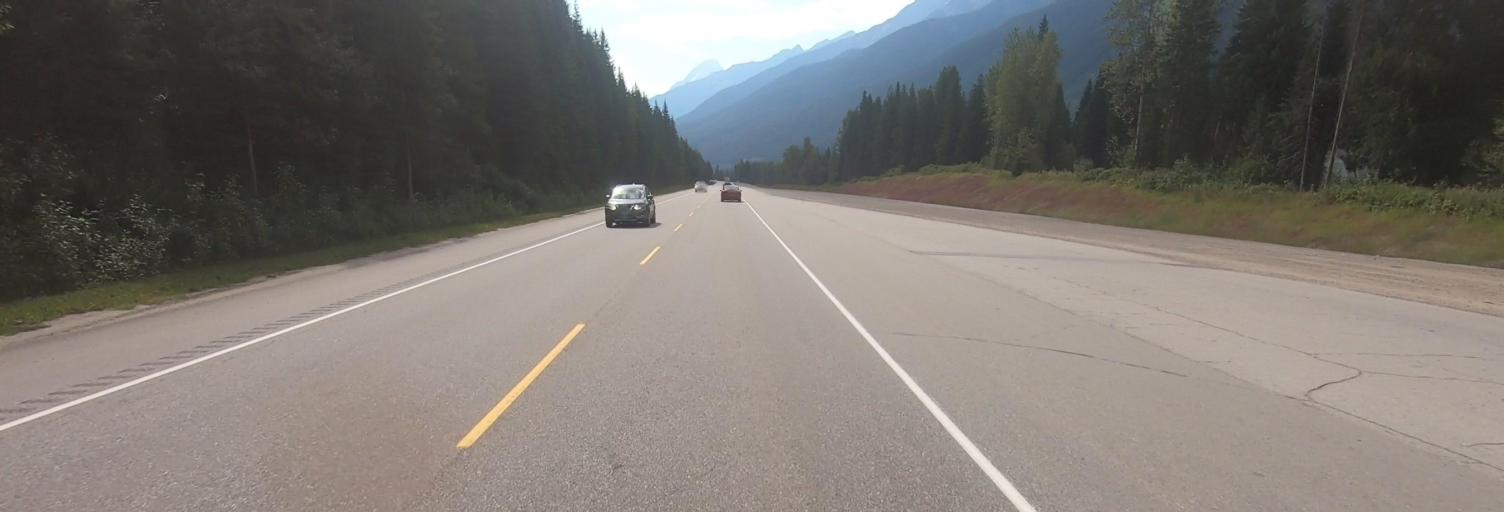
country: CA
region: British Columbia
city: Golden
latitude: 51.4160
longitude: -117.4729
